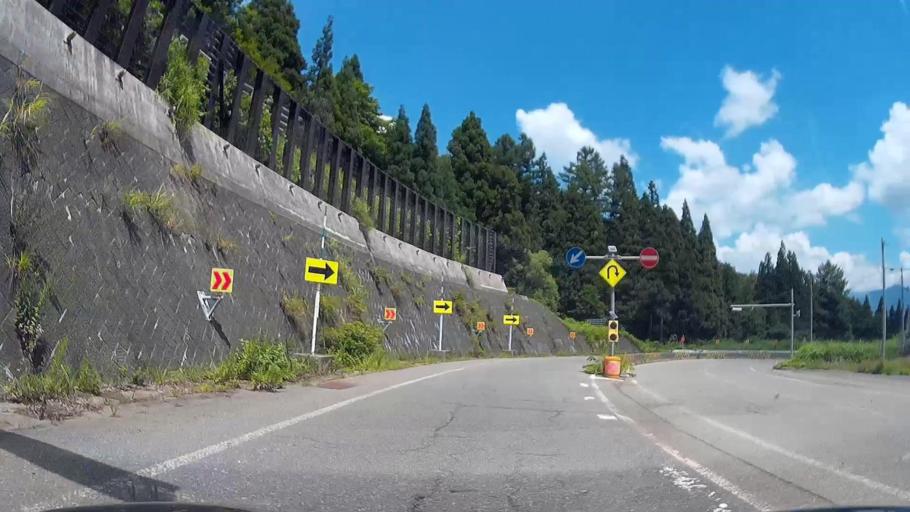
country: JP
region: Niigata
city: Shiozawa
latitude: 36.9139
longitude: 138.7965
